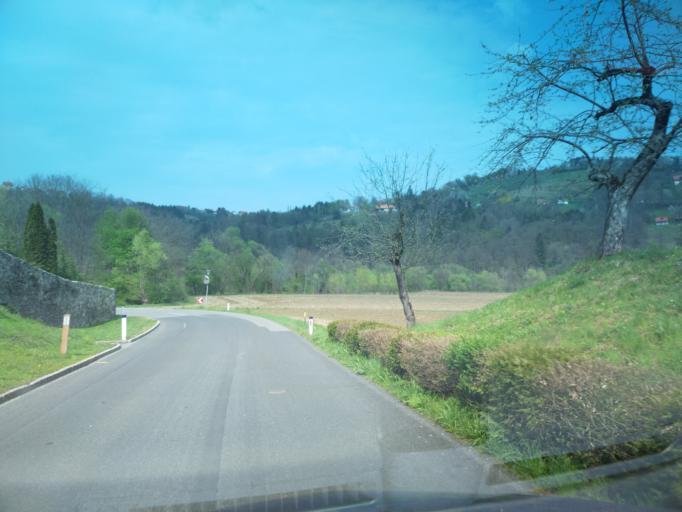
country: AT
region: Styria
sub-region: Politischer Bezirk Leibnitz
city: Kitzeck im Sausal
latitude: 46.7574
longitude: 15.4088
